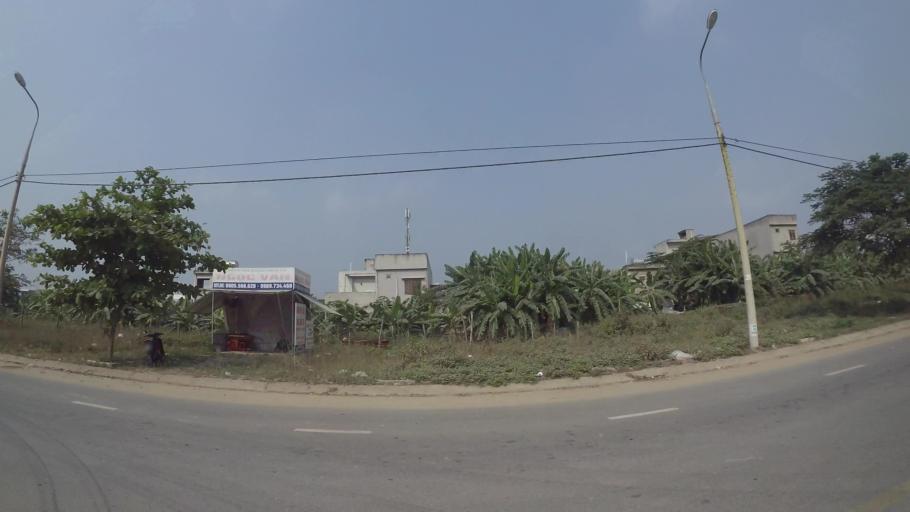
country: VN
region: Da Nang
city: Cam Le
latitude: 15.9974
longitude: 108.2162
